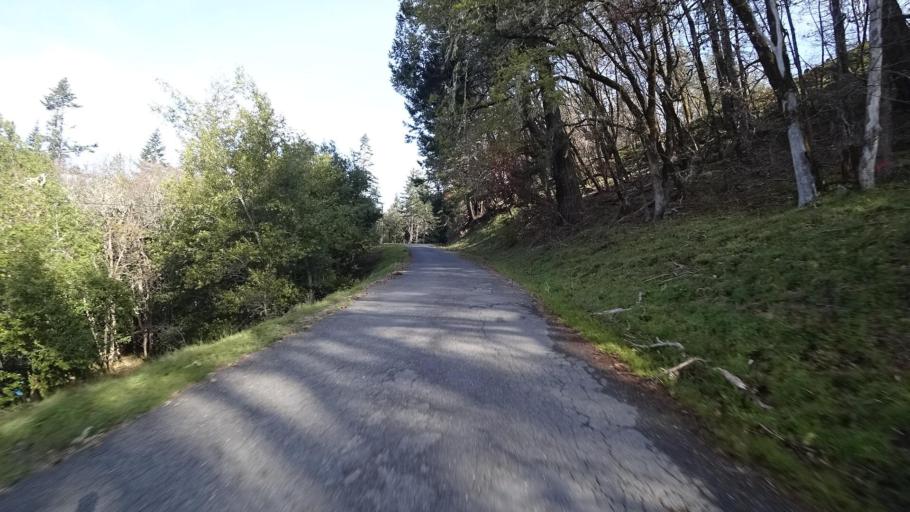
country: US
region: California
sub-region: Humboldt County
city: Hydesville
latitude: 40.6476
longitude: -123.9229
